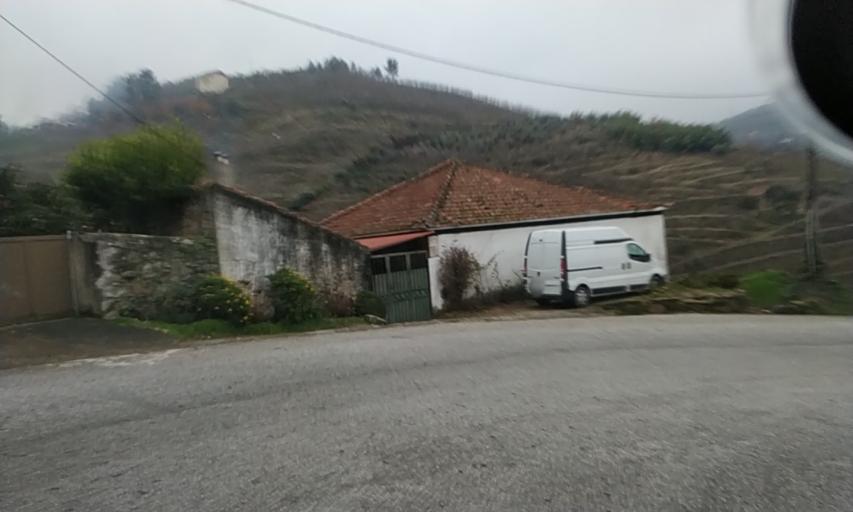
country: PT
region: Viseu
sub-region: Lamego
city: Lamego
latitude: 41.1176
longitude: -7.8039
